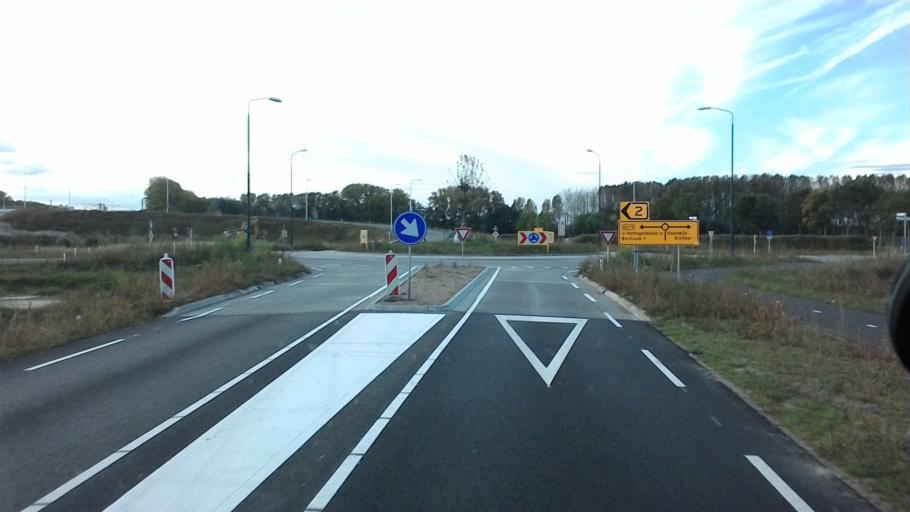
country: NL
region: North Brabant
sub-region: Gemeente Schijndel
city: Schijndel
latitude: 51.6459
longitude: 5.4605
